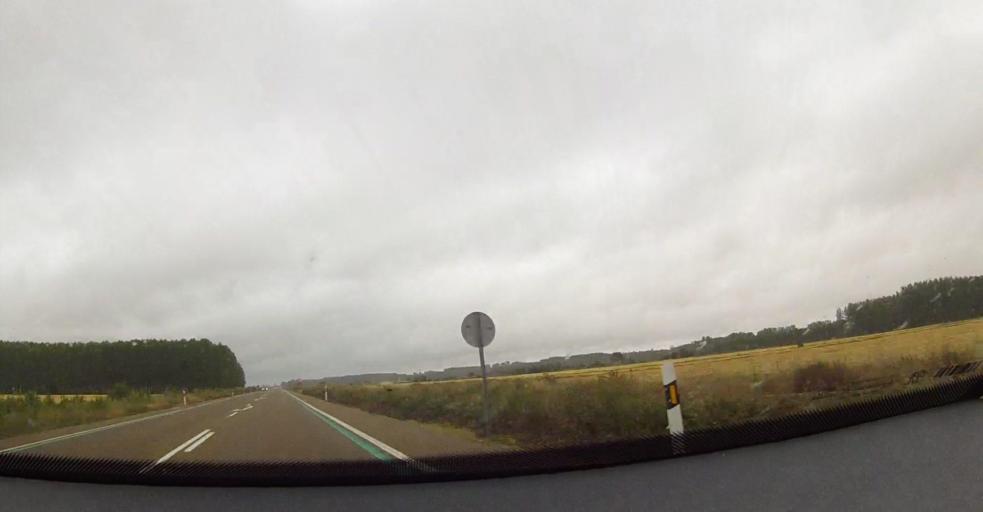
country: ES
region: Castille and Leon
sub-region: Provincia de Palencia
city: Carrion de los Condes
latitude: 42.3537
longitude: -4.6261
